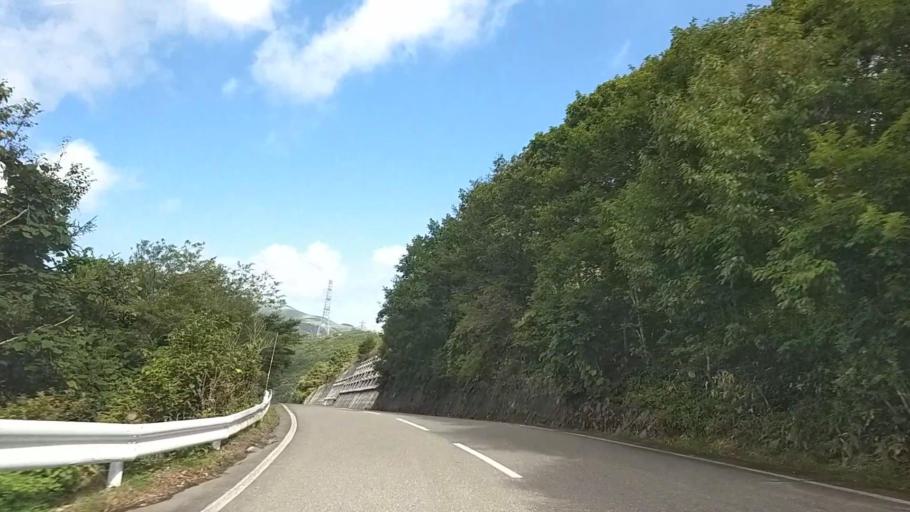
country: JP
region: Nagano
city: Suwa
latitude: 36.1367
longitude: 138.1517
